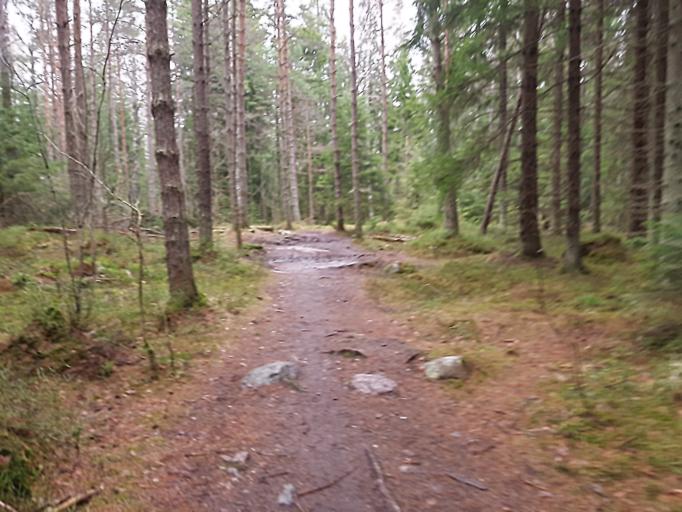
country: FI
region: Uusimaa
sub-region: Helsinki
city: Helsinki
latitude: 60.2615
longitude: 24.9212
